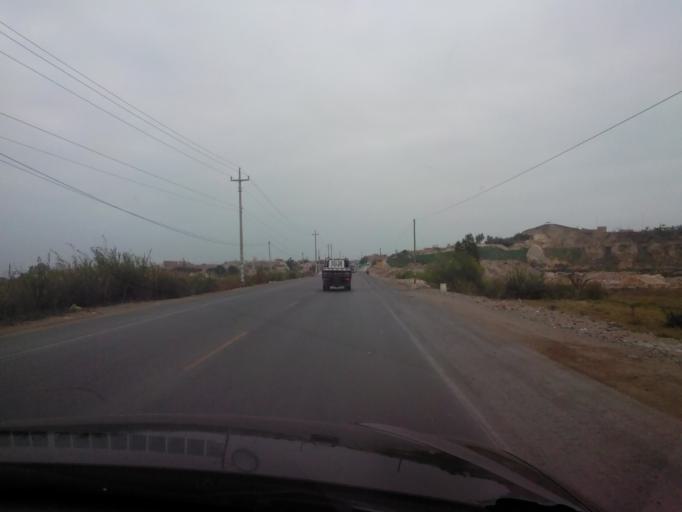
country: PE
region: Ica
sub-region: Provincia de Pisco
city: Villa Tupac Amaru
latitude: -13.6904
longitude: -76.1566
